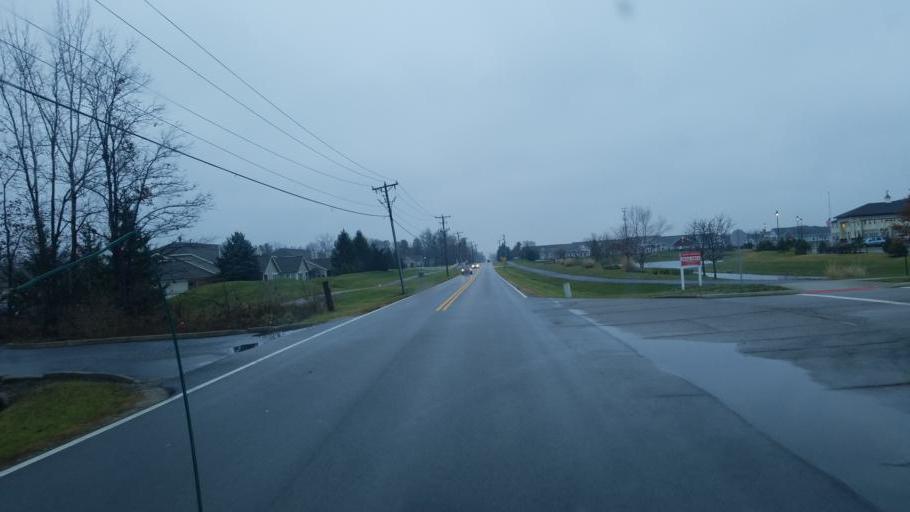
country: US
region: Ohio
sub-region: Delaware County
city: Powell
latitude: 40.1569
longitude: -83.0885
